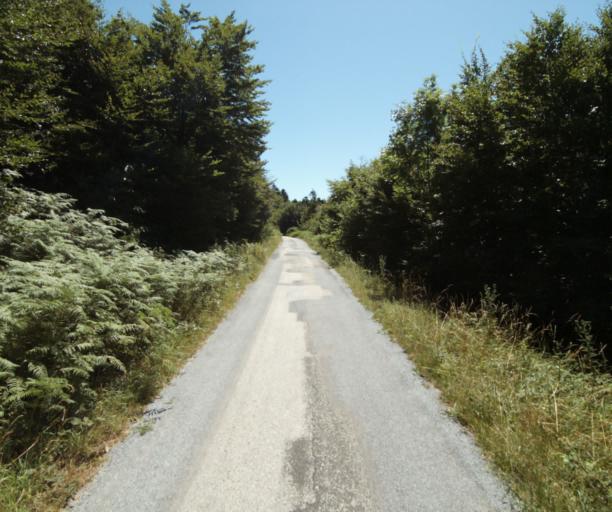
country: FR
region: Languedoc-Roussillon
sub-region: Departement de l'Aude
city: Cuxac-Cabardes
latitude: 43.4061
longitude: 2.2019
